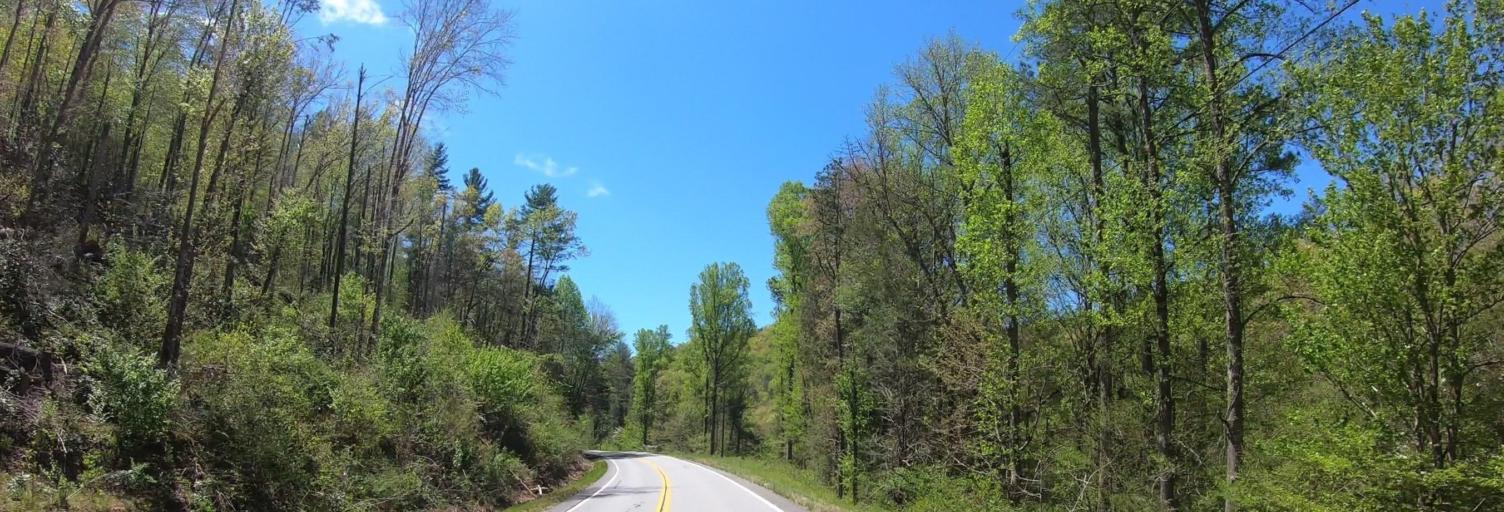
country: US
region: Georgia
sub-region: White County
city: Cleveland
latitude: 34.7679
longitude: -83.7488
